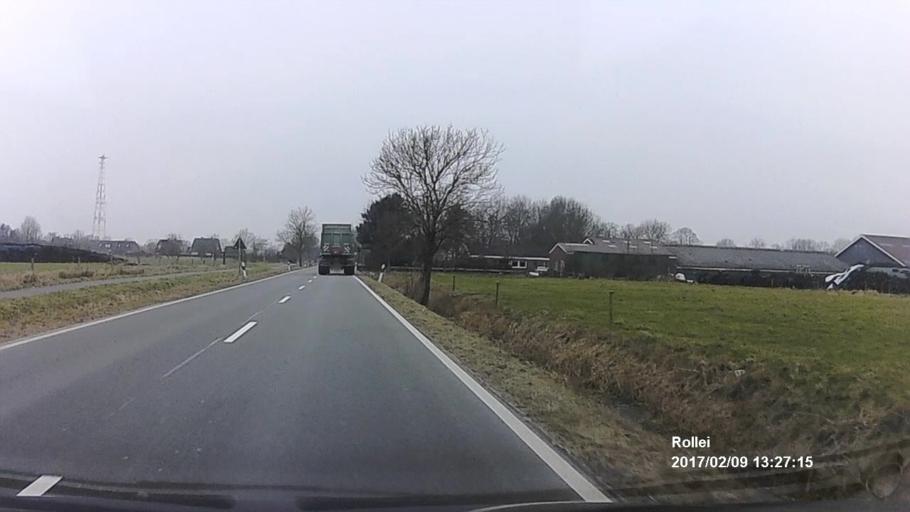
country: DE
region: Lower Saxony
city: Wirdum
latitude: 53.4848
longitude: 7.1303
